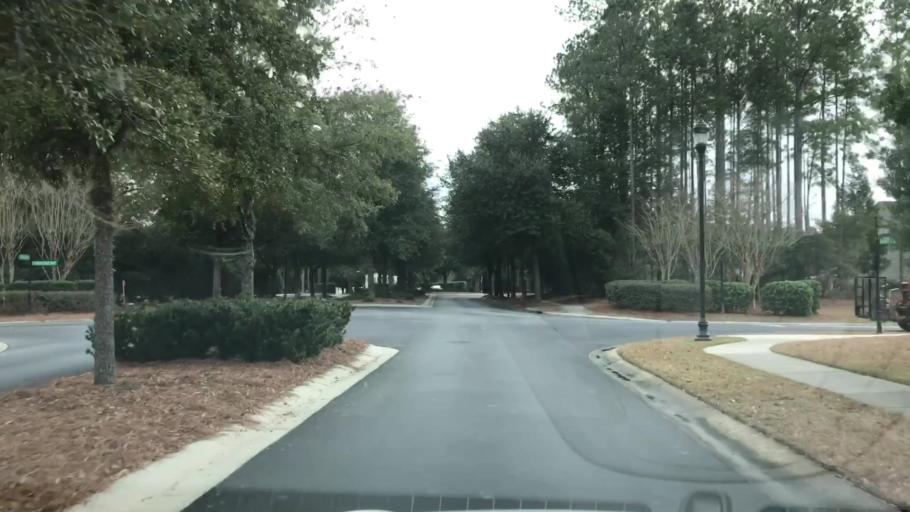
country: US
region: South Carolina
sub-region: Beaufort County
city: Bluffton
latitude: 32.2767
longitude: -80.9308
